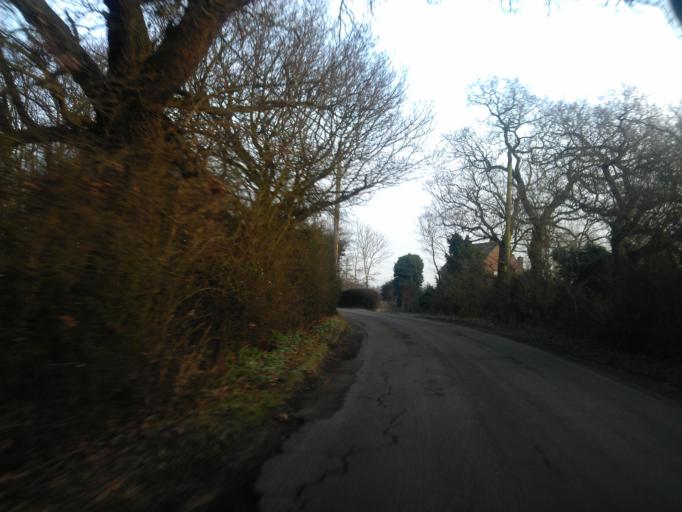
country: GB
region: England
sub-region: Essex
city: Wivenhoe
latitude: 51.8635
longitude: 0.9764
